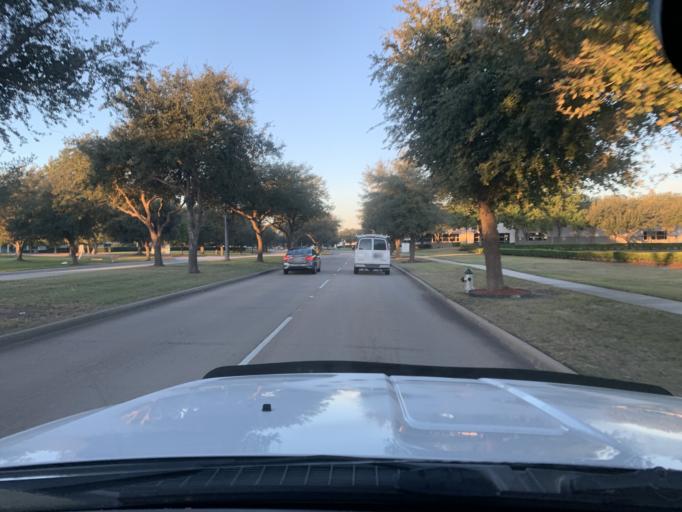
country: US
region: Texas
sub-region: Fort Bend County
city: Meadows Place
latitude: 29.6475
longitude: -95.6017
